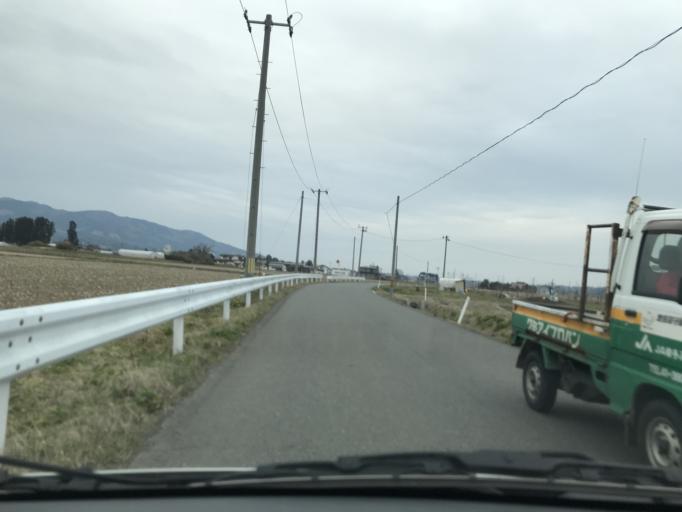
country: JP
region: Iwate
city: Mizusawa
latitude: 39.0822
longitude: 141.1442
